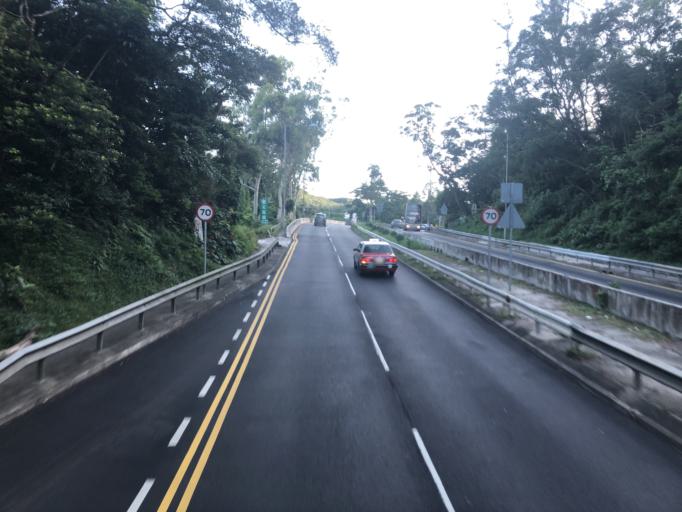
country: HK
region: Sai Kung
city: Sai Kung
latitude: 22.3359
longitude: 114.2420
